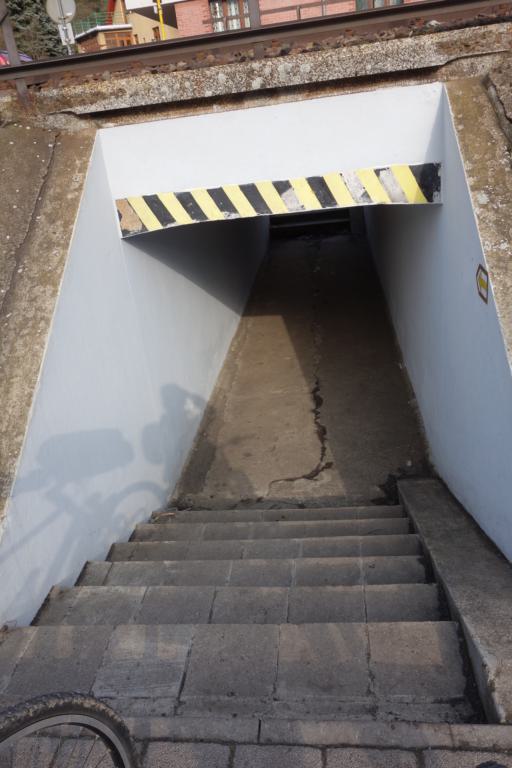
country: CZ
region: Ustecky
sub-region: Okres Usti nad Labem
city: Usti nad Labem
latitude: 50.6373
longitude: 14.0499
